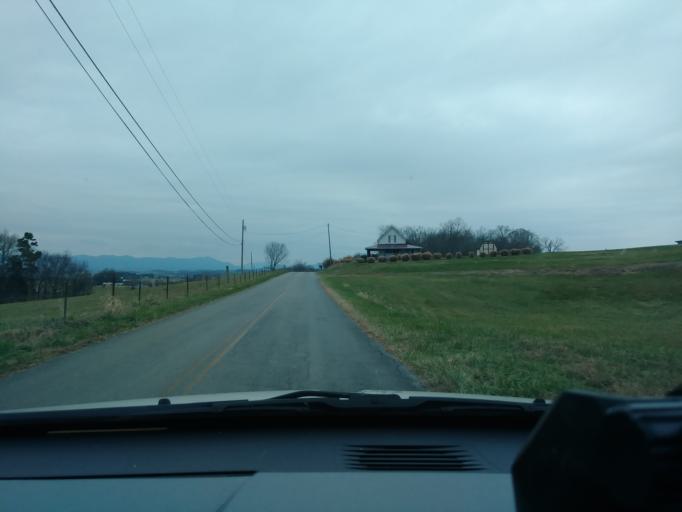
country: US
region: Tennessee
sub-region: Greene County
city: Greeneville
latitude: 36.0953
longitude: -82.8961
